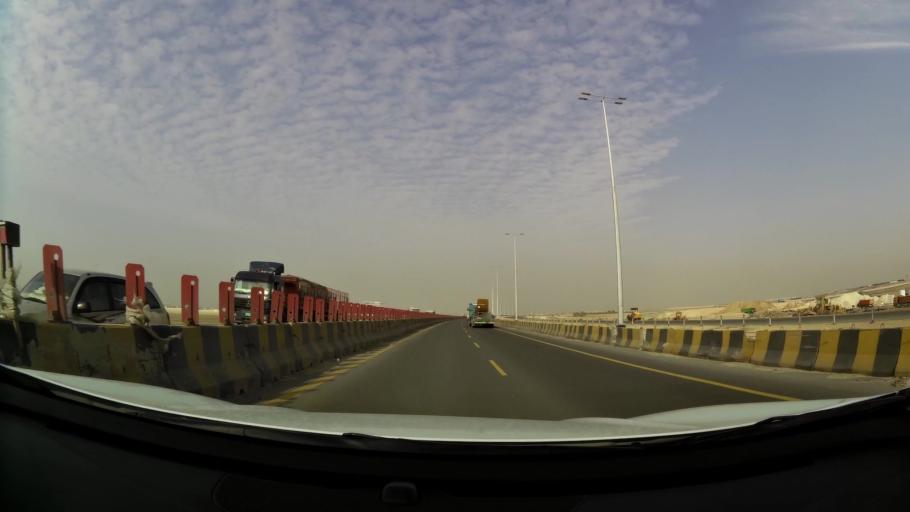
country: AE
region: Abu Dhabi
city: Abu Dhabi
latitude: 24.2657
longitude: 54.4937
